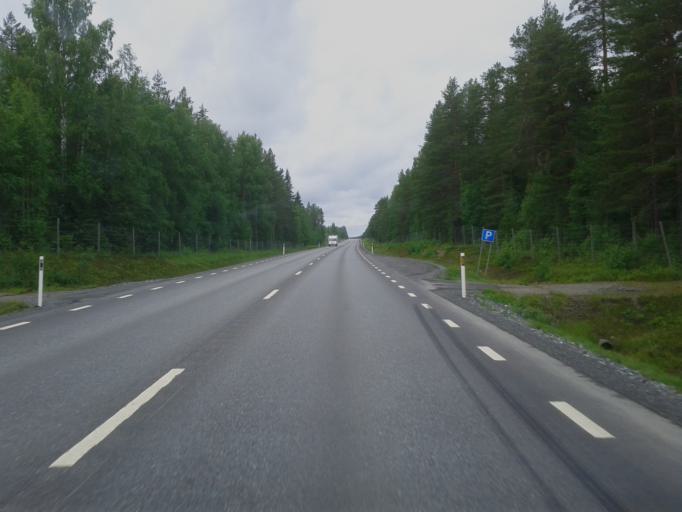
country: SE
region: Vaesterbotten
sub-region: Skelleftea Kommun
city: Forsbacka
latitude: 64.8438
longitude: 20.5021
